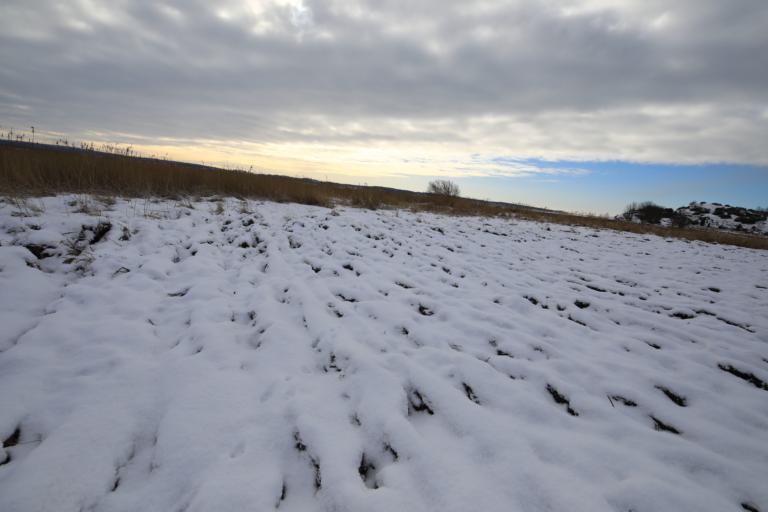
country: SE
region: Halland
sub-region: Kungsbacka Kommun
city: Frillesas
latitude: 57.2273
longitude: 12.2059
